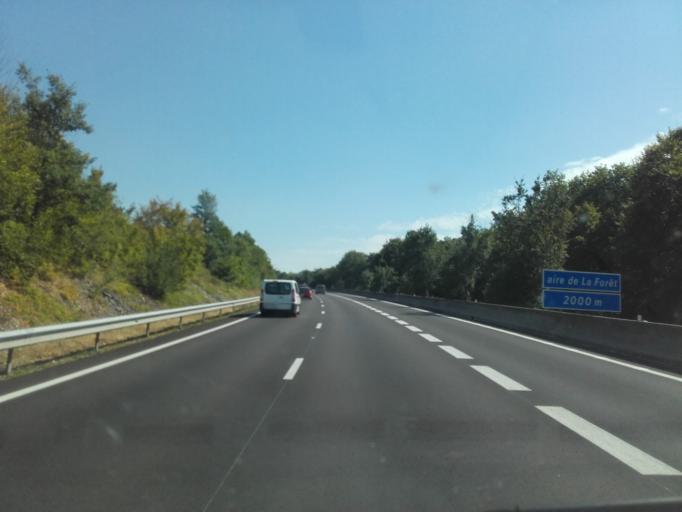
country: FR
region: Bourgogne
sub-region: Departement de la Cote-d'Or
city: Savigny-les-Beaune
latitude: 47.1250
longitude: 4.7000
